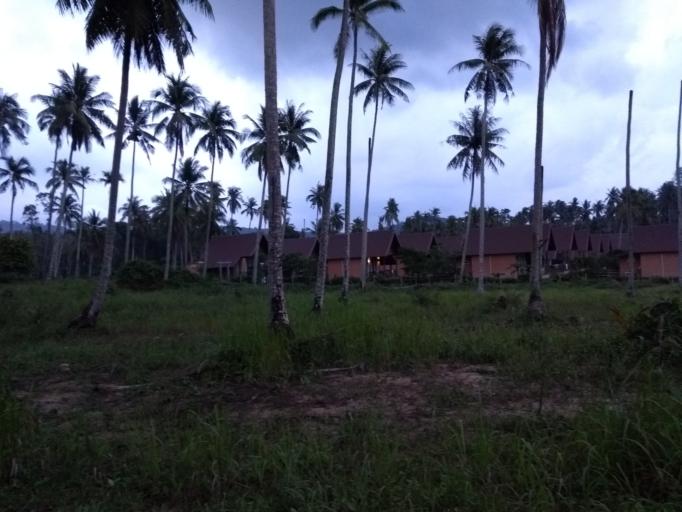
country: TH
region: Trat
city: Ko Kut
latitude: 11.6539
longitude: 102.5342
